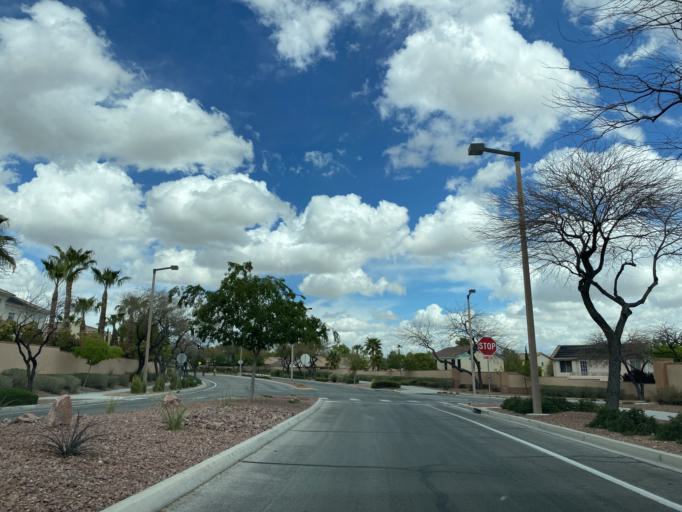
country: US
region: Nevada
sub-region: Clark County
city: Summerlin South
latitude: 36.1878
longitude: -115.3290
